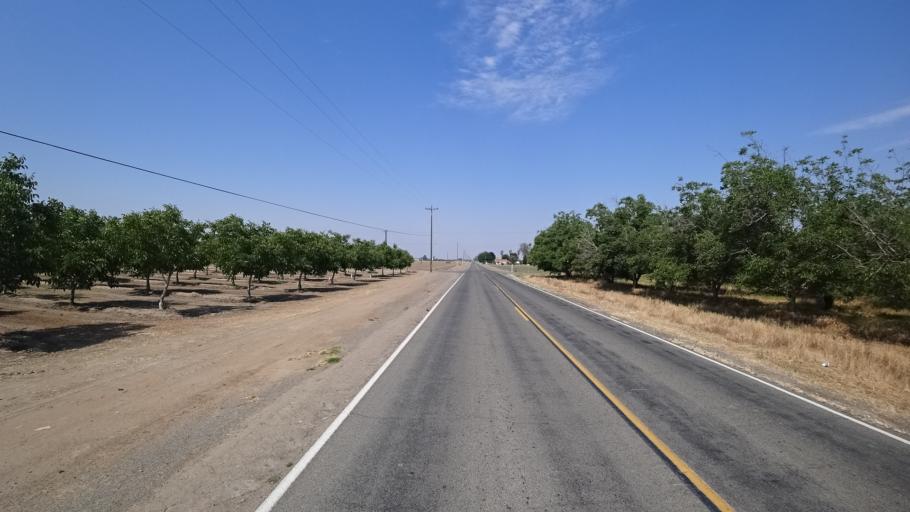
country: US
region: California
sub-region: Fresno County
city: Riverdale
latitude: 36.4020
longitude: -119.7796
